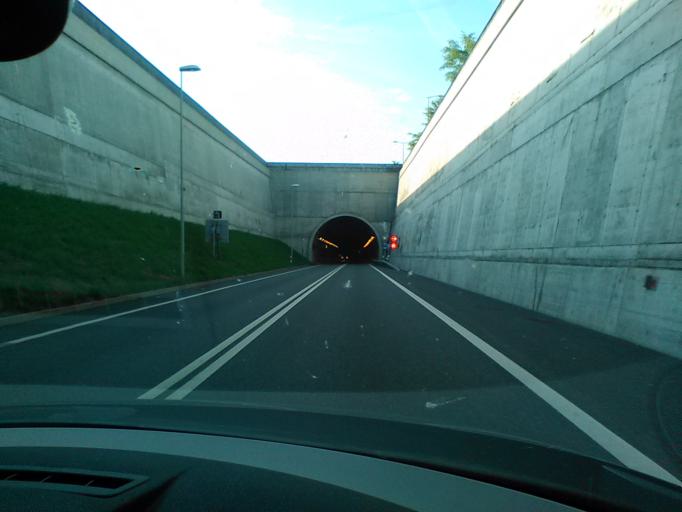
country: CH
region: Fribourg
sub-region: Gruyere District
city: Bulle
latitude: 46.6165
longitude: 7.0462
